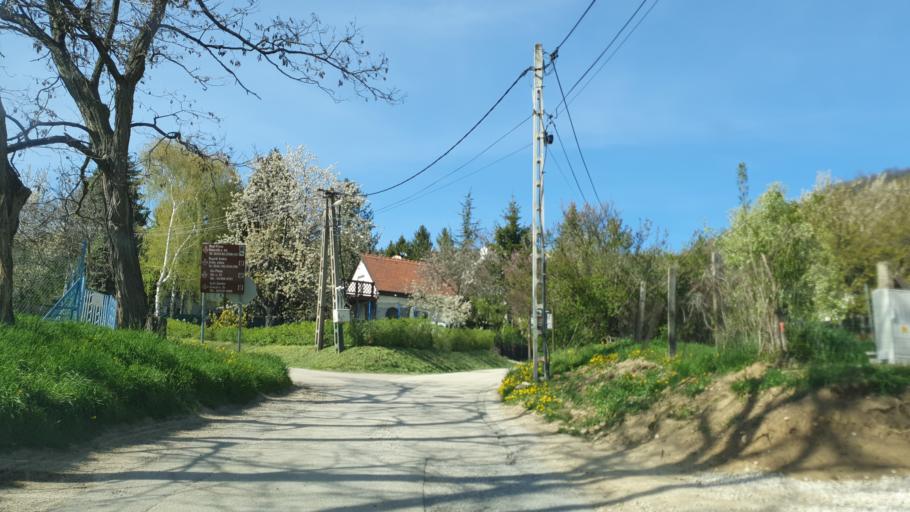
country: HU
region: Fejer
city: Bodajk
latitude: 47.3566
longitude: 18.2771
